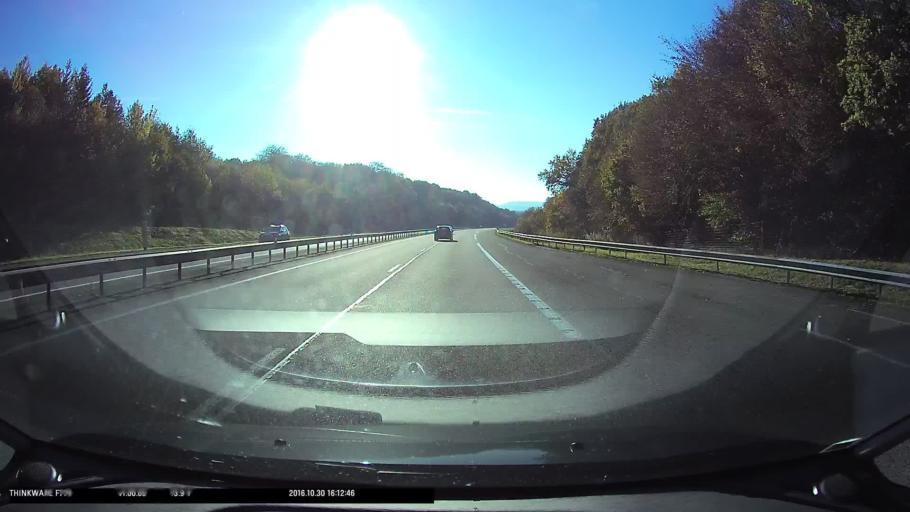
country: FR
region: Franche-Comte
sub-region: Departement du Doubs
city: Colombier-Fontaine
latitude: 47.4202
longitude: 6.6366
